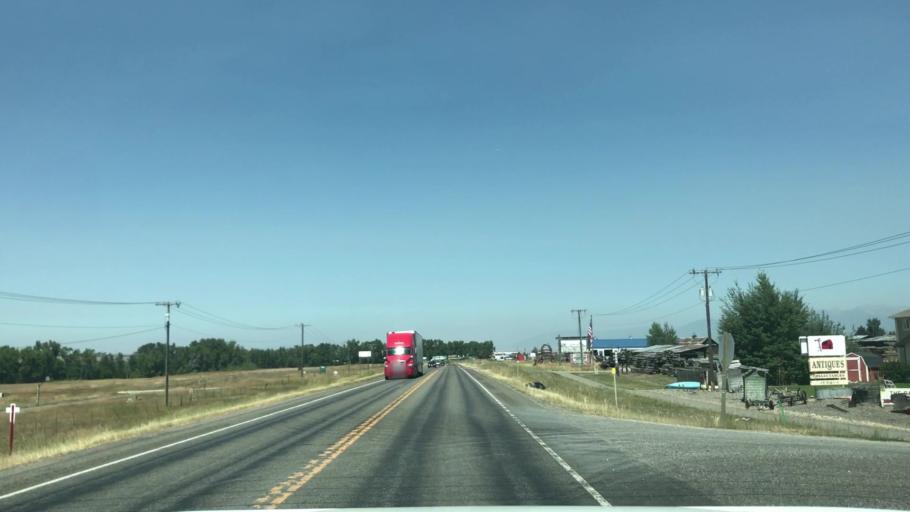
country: US
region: Montana
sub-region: Gallatin County
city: Four Corners
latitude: 45.6026
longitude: -111.1961
